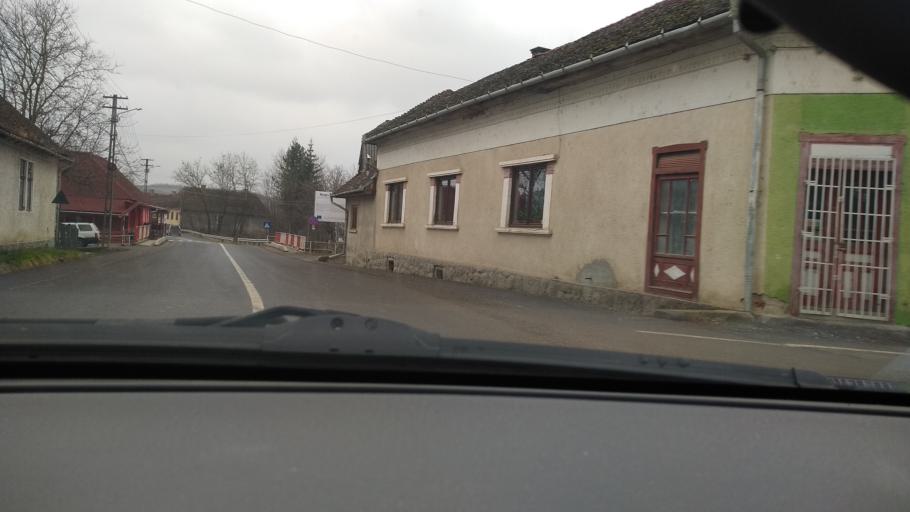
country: RO
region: Mures
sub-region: Comuna Magherani
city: Magherani
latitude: 46.5649
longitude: 24.9039
